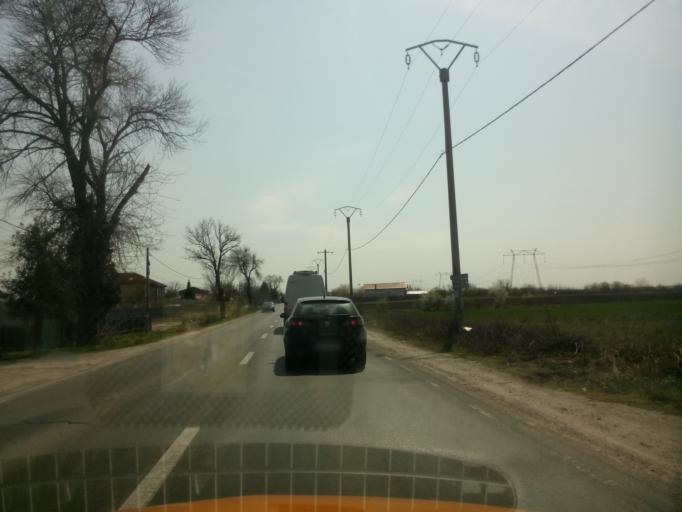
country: RO
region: Calarasi
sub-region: Comuna Frumusani
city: Frumusani
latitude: 44.3087
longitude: 26.2926
